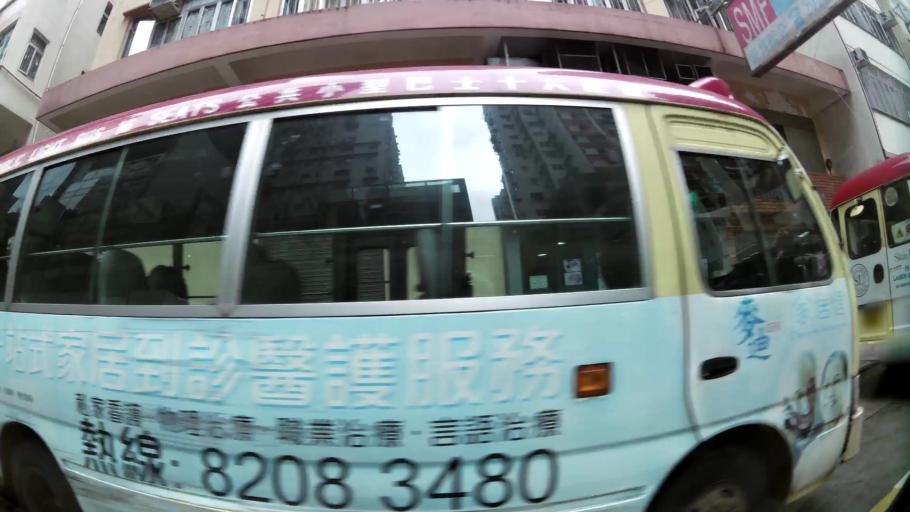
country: HK
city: Hong Kong
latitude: 22.2816
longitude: 114.1270
